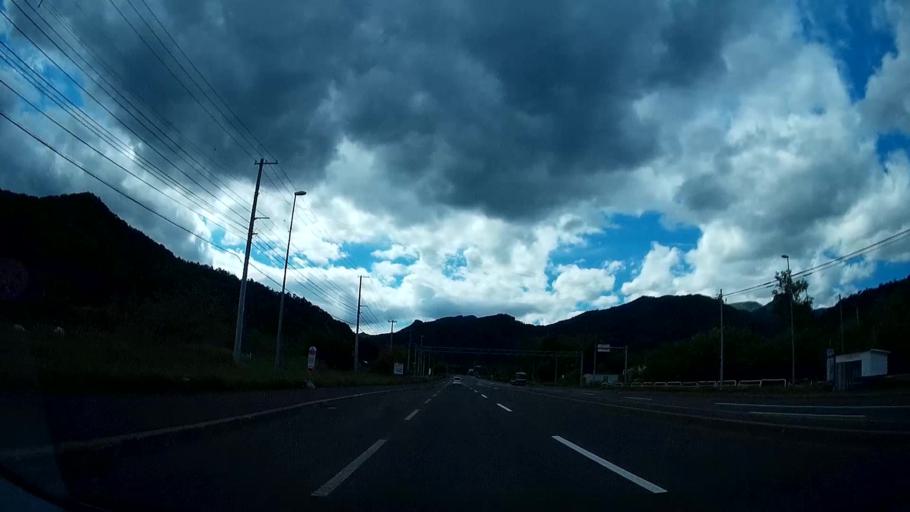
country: JP
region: Hokkaido
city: Sapporo
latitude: 42.9663
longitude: 141.2180
